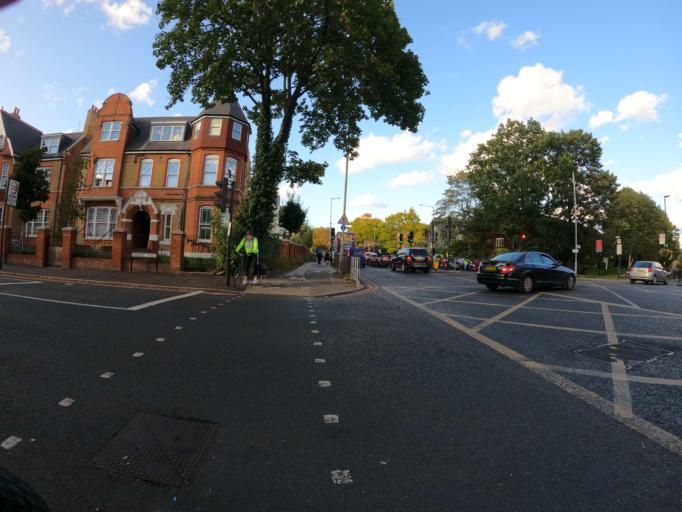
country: GB
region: England
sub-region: Greater London
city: Ealing Broadway
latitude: 51.5169
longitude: -0.2915
